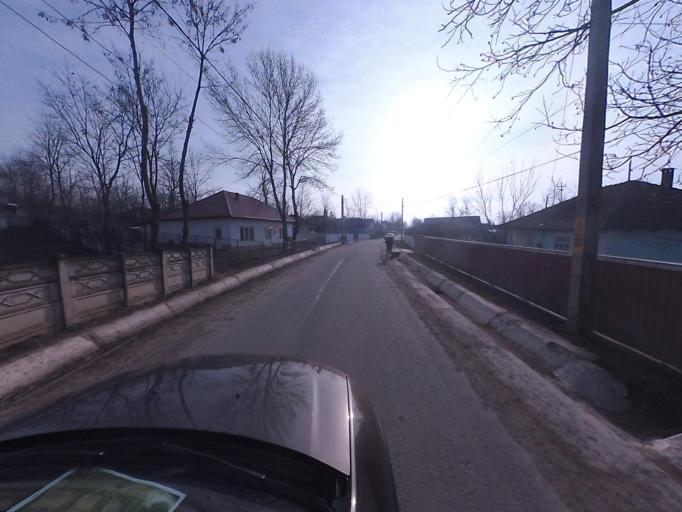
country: RO
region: Vaslui
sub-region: Comuna Solesti
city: Solesti
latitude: 46.8108
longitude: 27.7733
